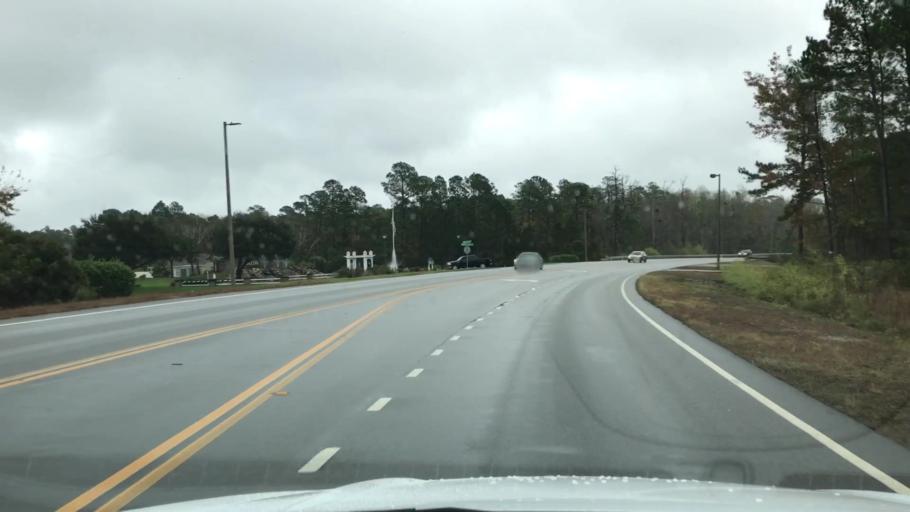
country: US
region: South Carolina
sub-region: Horry County
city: Forestbrook
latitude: 33.7597
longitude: -78.9195
